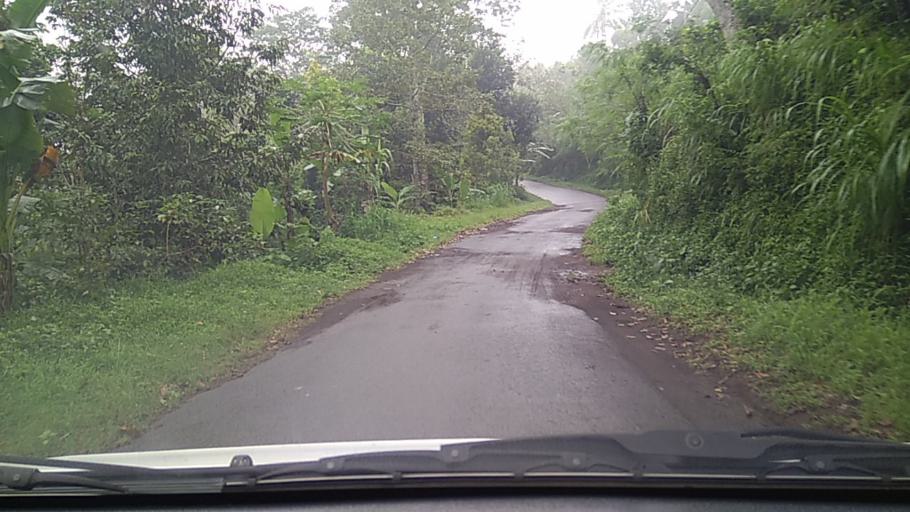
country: ID
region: Bali
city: Banjar Ambengan
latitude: -8.1981
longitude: 115.1789
